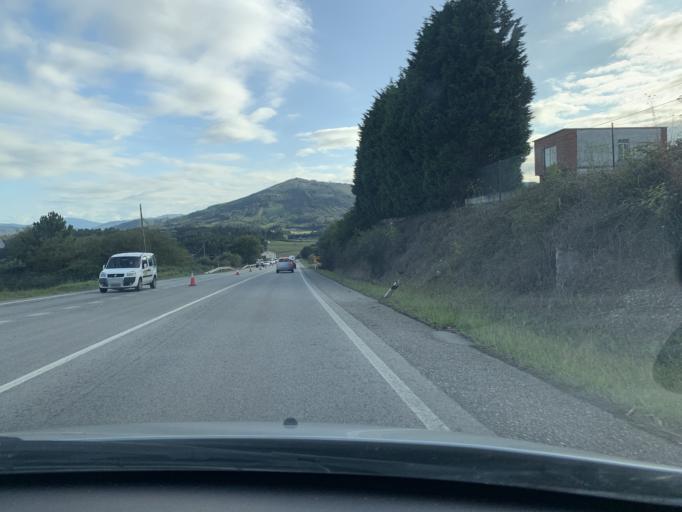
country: ES
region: Galicia
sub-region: Provincia de Lugo
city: Foz
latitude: 43.5502
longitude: -7.2675
